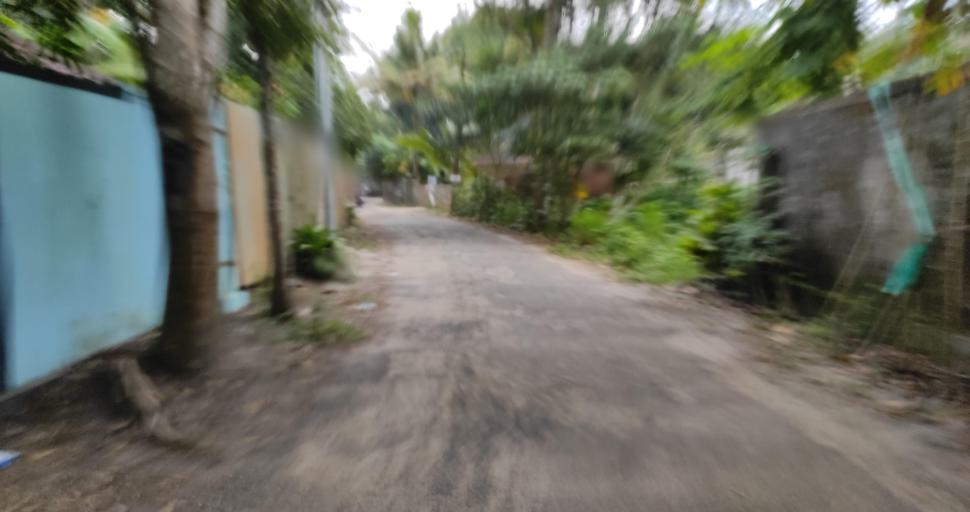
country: IN
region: Kerala
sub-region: Alappuzha
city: Shertallai
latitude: 9.6700
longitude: 76.3347
